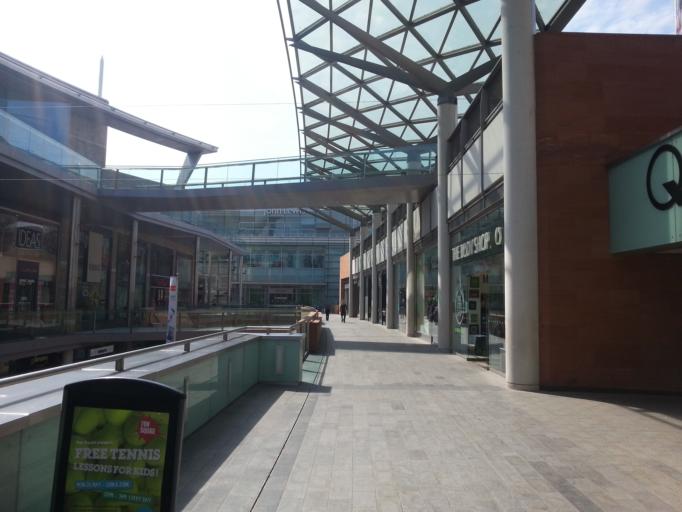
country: GB
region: England
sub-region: Liverpool
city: Liverpool
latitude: 53.4039
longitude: -2.9876
